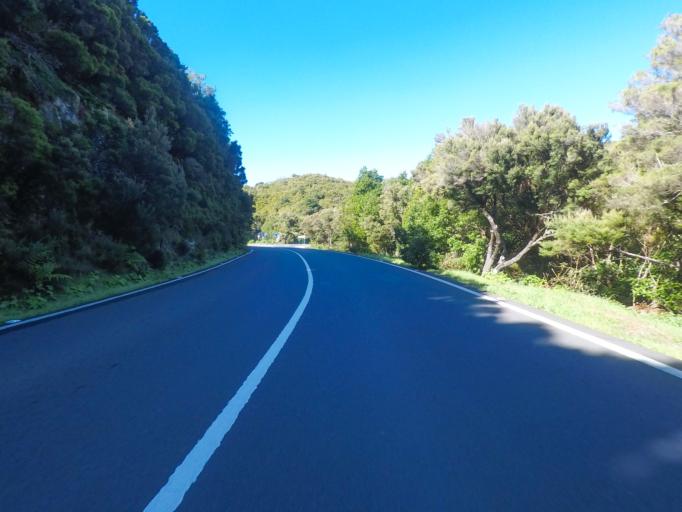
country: ES
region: Canary Islands
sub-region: Provincia de Santa Cruz de Tenerife
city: Alajero
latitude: 28.1086
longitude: -17.2410
